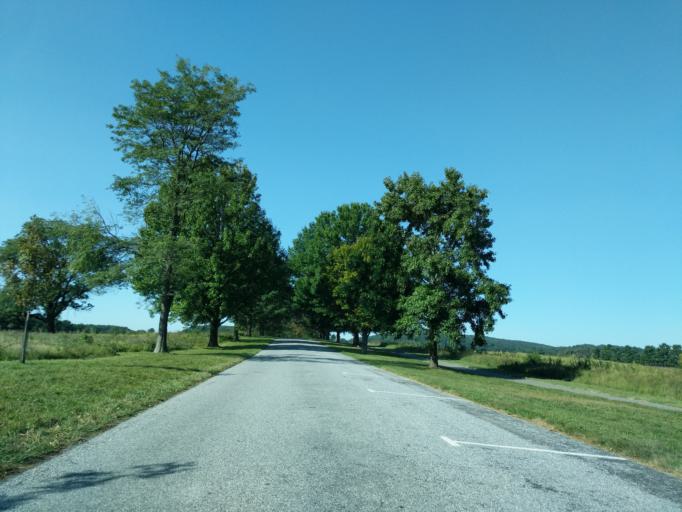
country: US
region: Pennsylvania
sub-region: Montgomery County
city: Audubon
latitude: 40.0962
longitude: -75.4277
